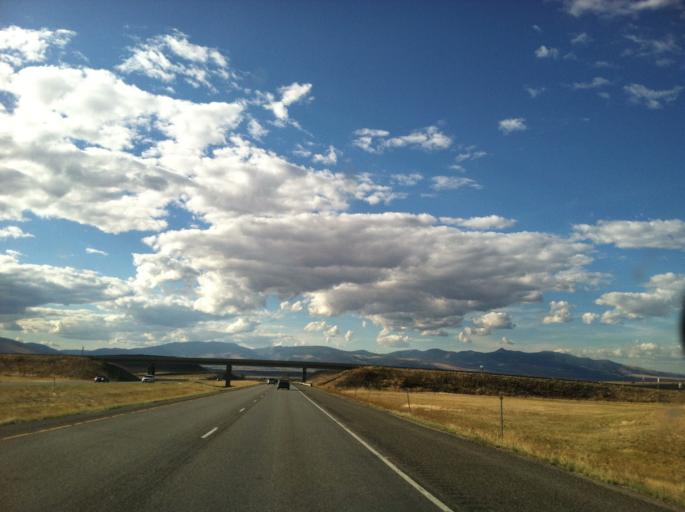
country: US
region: Montana
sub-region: Deer Lodge County
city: Warm Springs
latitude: 46.0530
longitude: -112.7555
